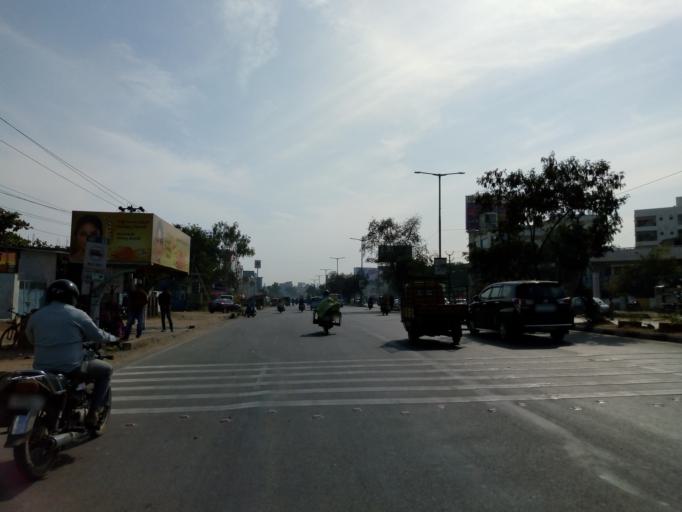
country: IN
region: Telangana
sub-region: Rangareddi
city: Lal Bahadur Nagar
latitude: 17.3690
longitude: 78.5574
